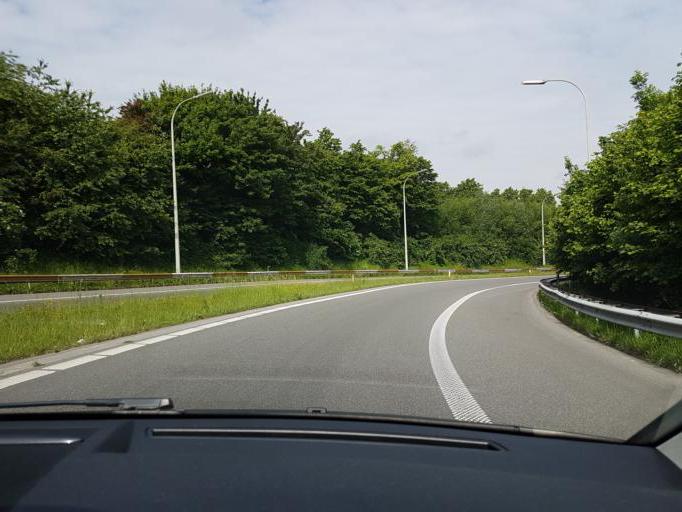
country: BE
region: Flanders
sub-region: Provincie Vlaams-Brabant
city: Dilbeek
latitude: 50.8652
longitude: 4.2683
